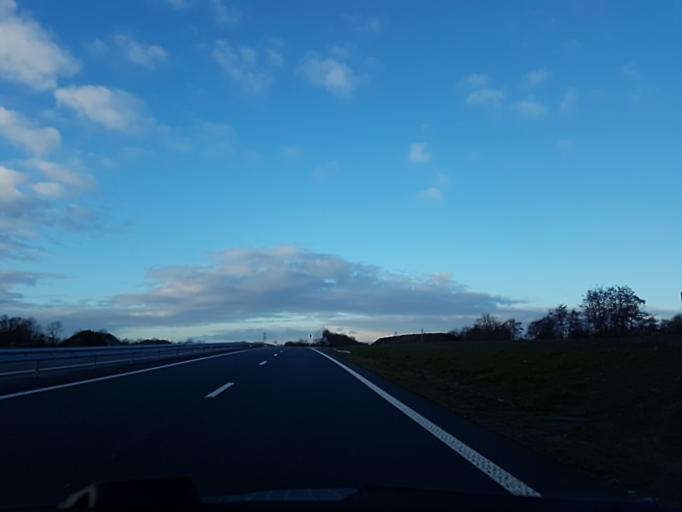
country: NL
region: Friesland
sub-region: Gemeente Tytsjerksteradiel
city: Burgum
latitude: 53.1926
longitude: 5.9769
